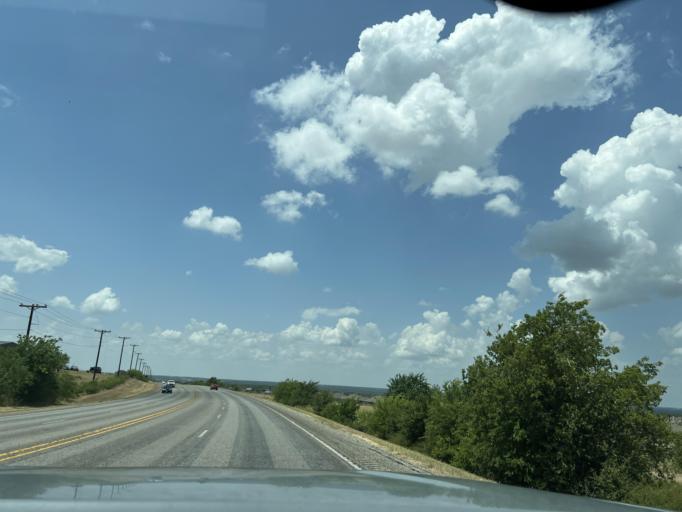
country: US
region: Texas
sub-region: Parker County
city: Springtown
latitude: 32.9098
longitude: -97.7201
